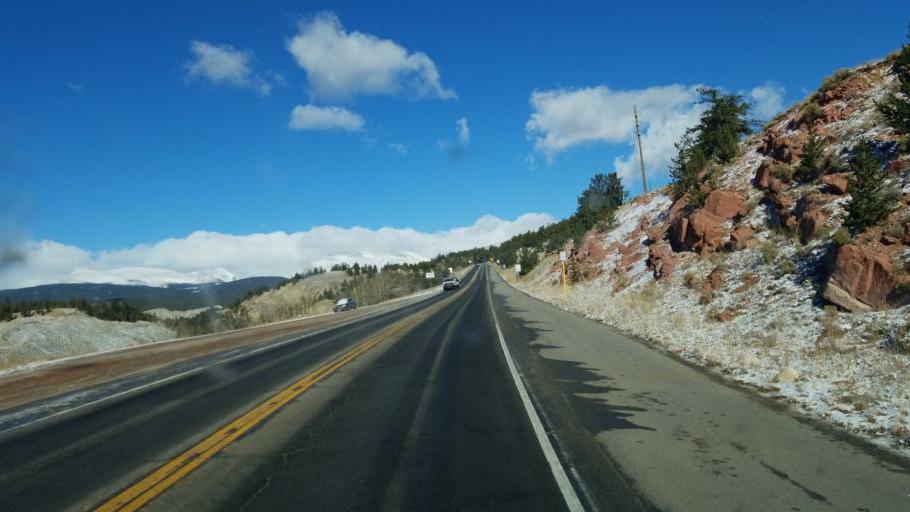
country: US
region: Colorado
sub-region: Park County
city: Fairplay
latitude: 39.2266
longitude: -106.0061
